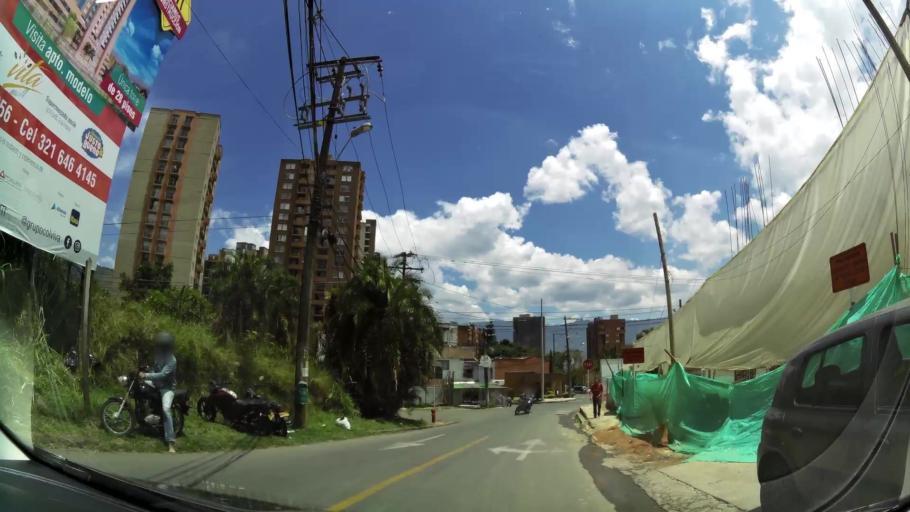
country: CO
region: Antioquia
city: La Estrella
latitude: 6.1642
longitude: -75.6366
